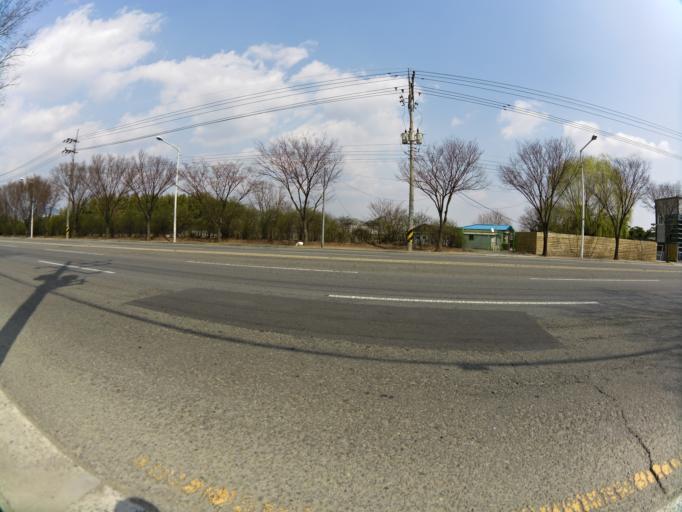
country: KR
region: Gyeongsangbuk-do
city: Gyeongsan-si
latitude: 35.8571
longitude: 128.7205
